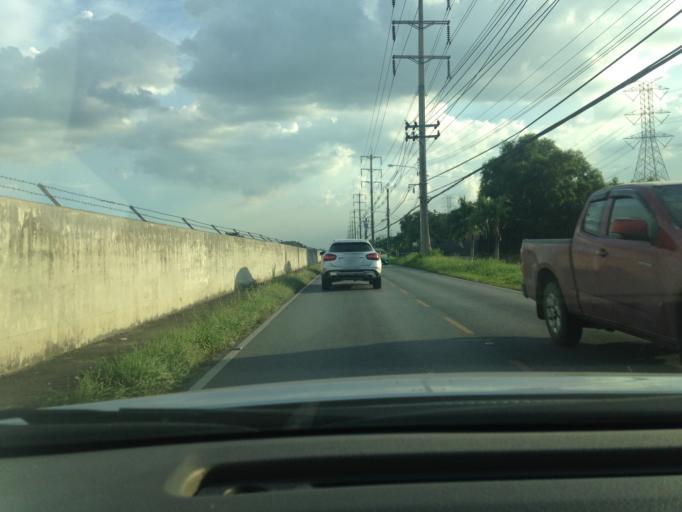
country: TH
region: Bangkok
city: Don Mueang
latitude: 13.9254
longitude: 100.5614
